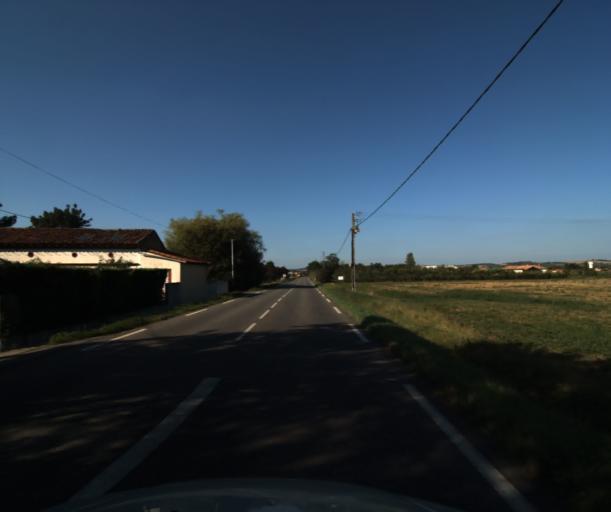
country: FR
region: Midi-Pyrenees
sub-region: Departement de la Haute-Garonne
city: Labarthe-sur-Leze
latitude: 43.4463
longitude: 1.3857
